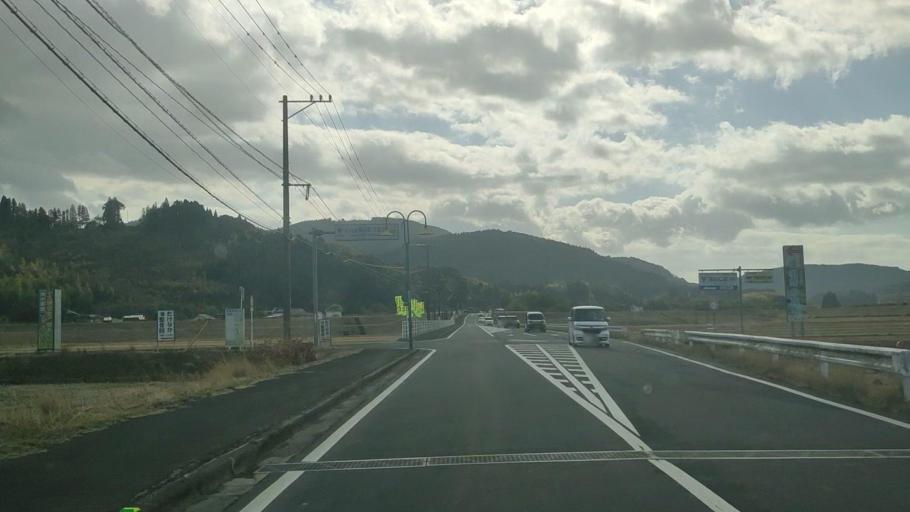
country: JP
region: Kagoshima
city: Okuchi-shinohara
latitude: 31.9973
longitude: 130.7486
